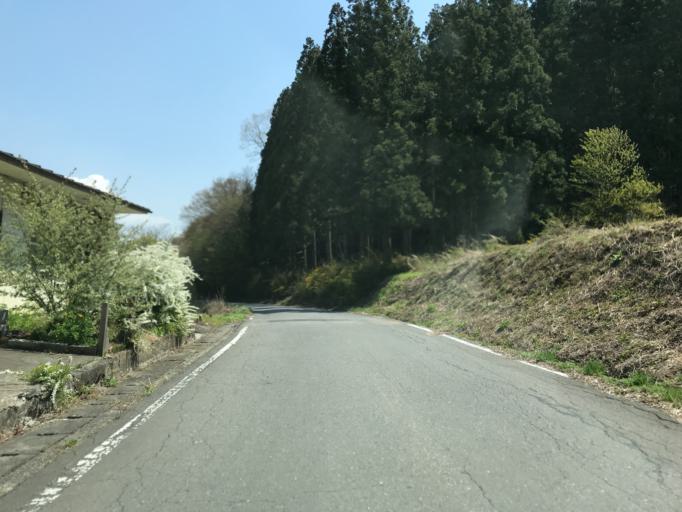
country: JP
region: Ibaraki
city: Kitaibaraki
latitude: 36.9670
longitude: 140.6574
